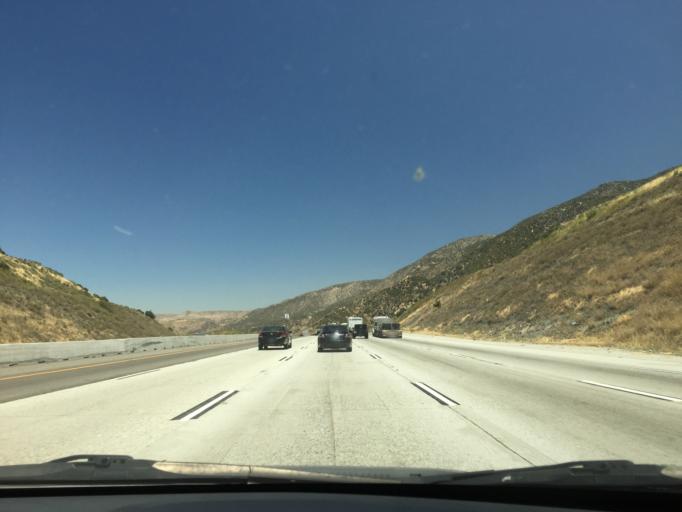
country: US
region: California
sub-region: San Bernardino County
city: Oak Hills
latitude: 34.2612
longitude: -117.4495
